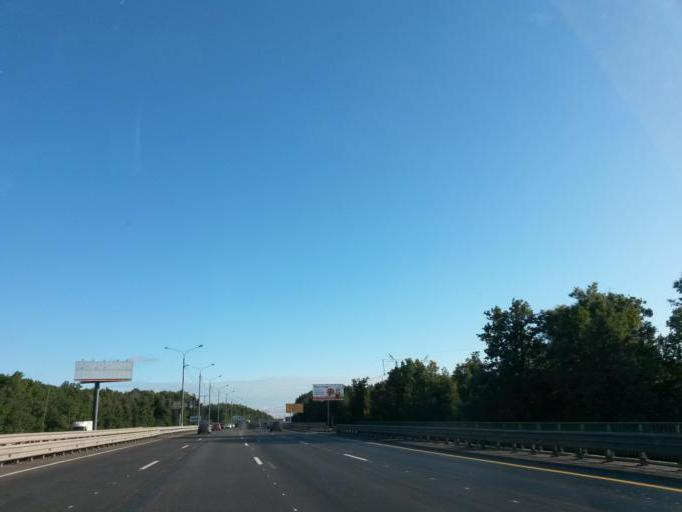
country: RU
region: Moscow
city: Annino
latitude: 55.5441
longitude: 37.6072
